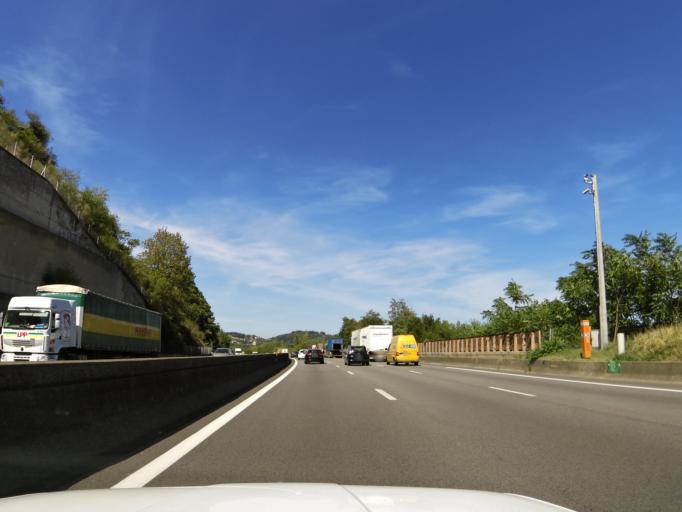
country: FR
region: Rhone-Alpes
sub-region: Departement du Rhone
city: Sainte-Colombe
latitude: 45.5257
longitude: 4.8615
